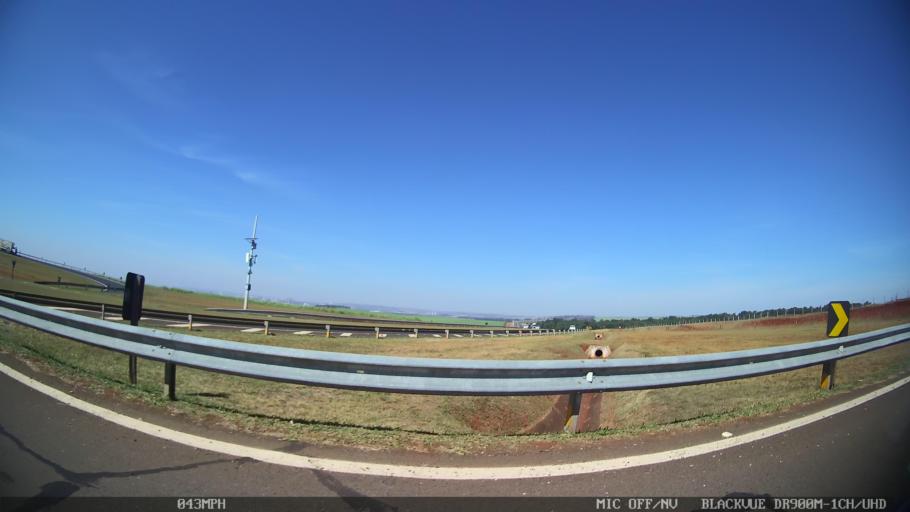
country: BR
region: Sao Paulo
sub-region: Ribeirao Preto
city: Ribeirao Preto
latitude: -21.1675
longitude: -47.9002
